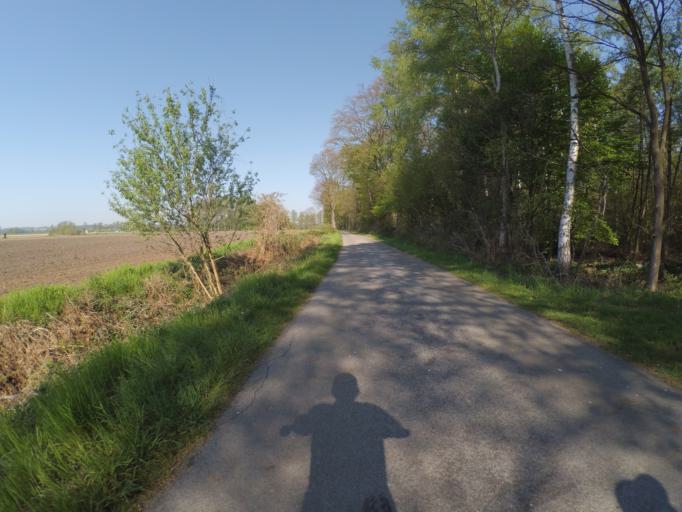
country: DE
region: North Rhine-Westphalia
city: Ludinghausen
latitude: 51.7923
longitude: 7.4152
